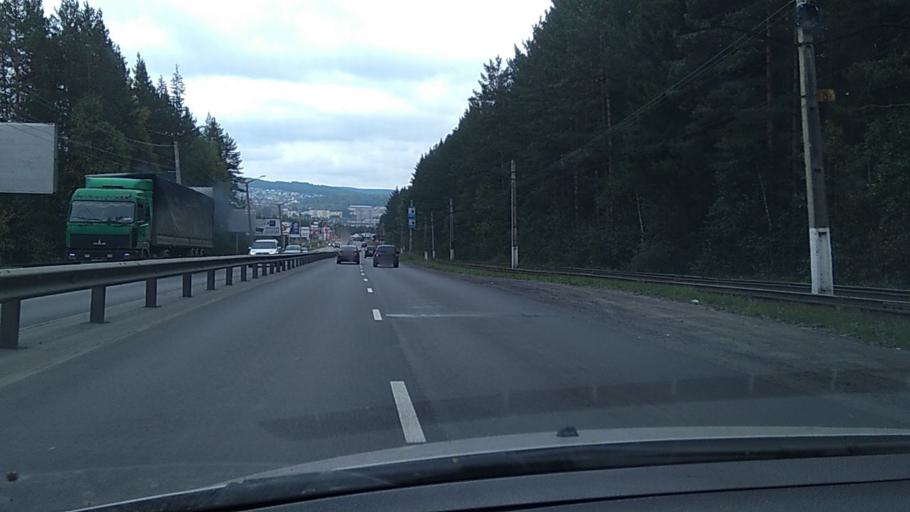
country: RU
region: Chelyabinsk
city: Zlatoust
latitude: 55.1286
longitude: 59.6880
